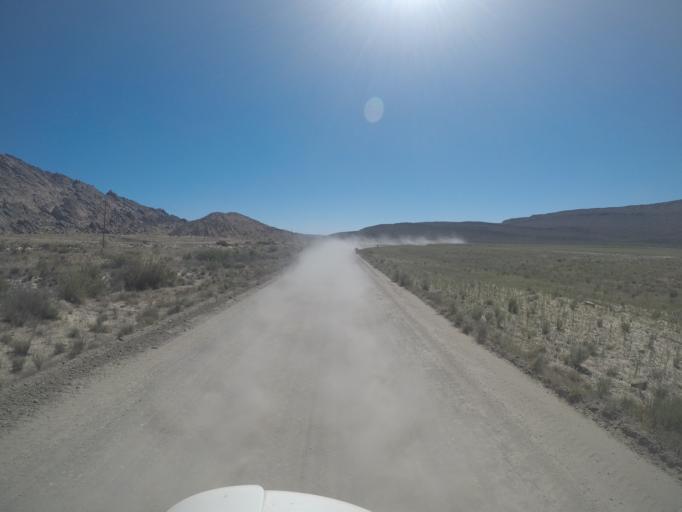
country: ZA
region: Western Cape
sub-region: Cape Winelands District Municipality
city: Ceres
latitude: -32.8329
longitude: 19.4511
